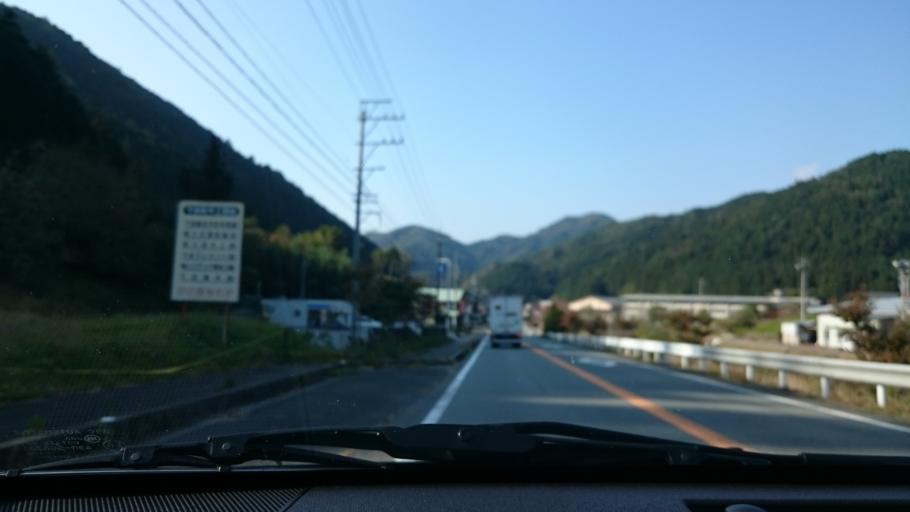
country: JP
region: Gifu
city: Gujo
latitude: 35.7650
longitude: 137.2884
